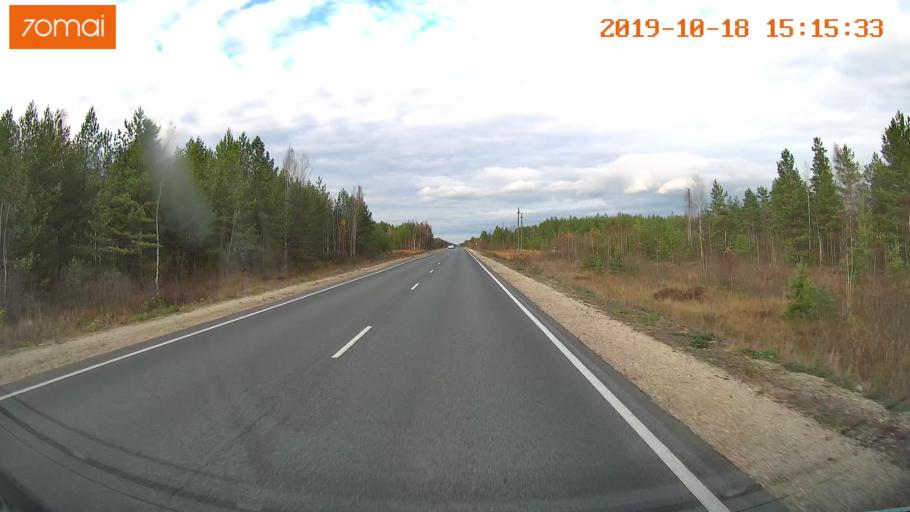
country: RU
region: Vladimir
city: Gus'-Khrustal'nyy
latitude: 55.6210
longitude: 40.7228
